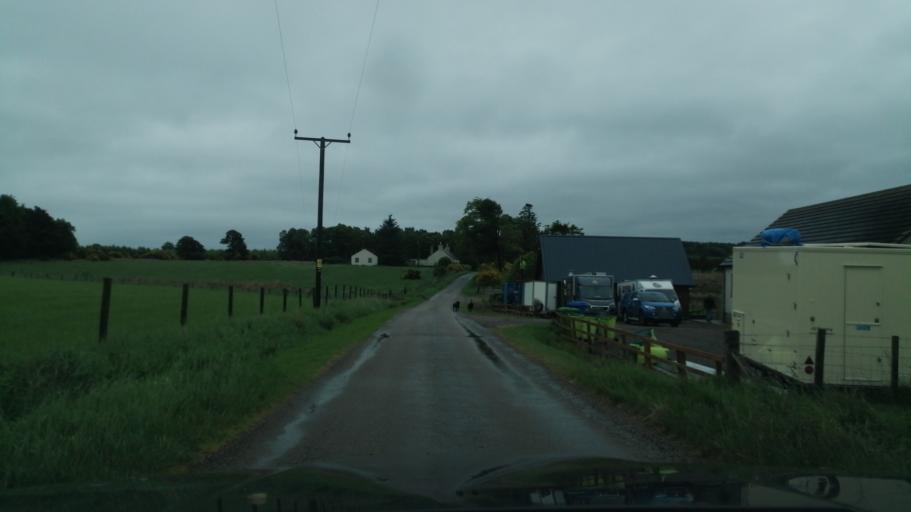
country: GB
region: Scotland
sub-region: Moray
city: Keith
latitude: 57.5693
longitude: -2.8610
